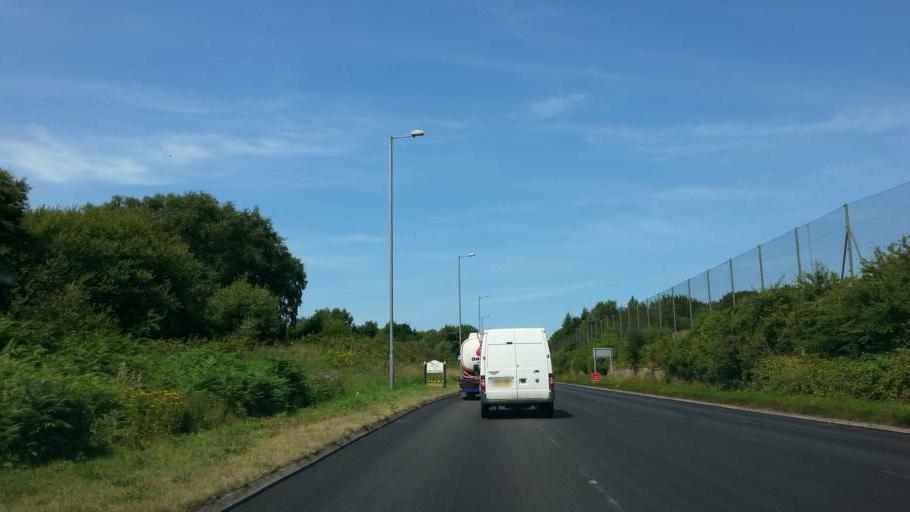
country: GB
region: England
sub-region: Staffordshire
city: Chasetown
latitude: 52.6682
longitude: -1.9402
